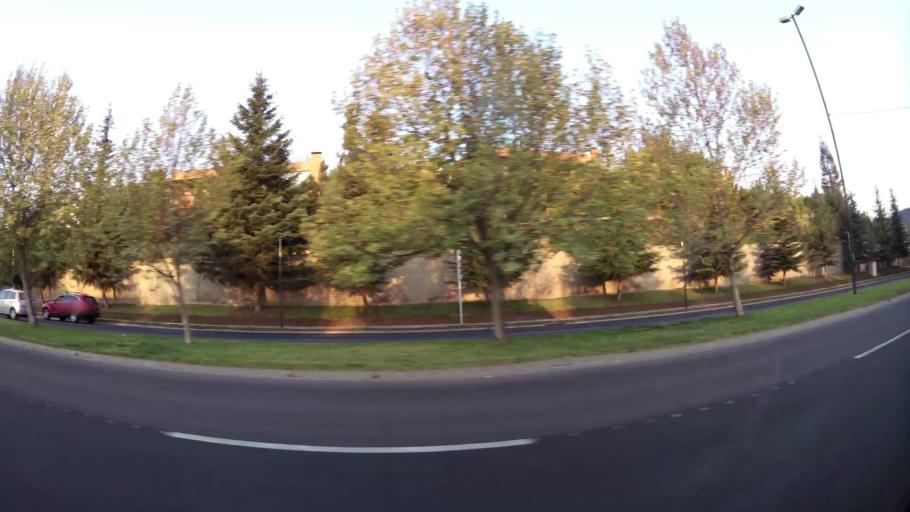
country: CL
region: Santiago Metropolitan
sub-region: Provincia de Chacabuco
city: Chicureo Abajo
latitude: -33.3274
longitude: -70.5426
